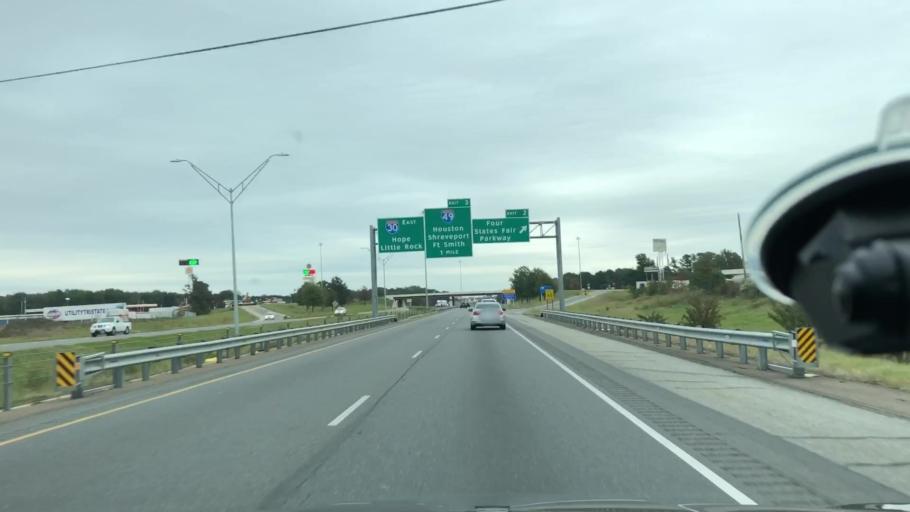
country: US
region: Arkansas
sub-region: Miller County
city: Texarkana
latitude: 33.4748
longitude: -94.0117
